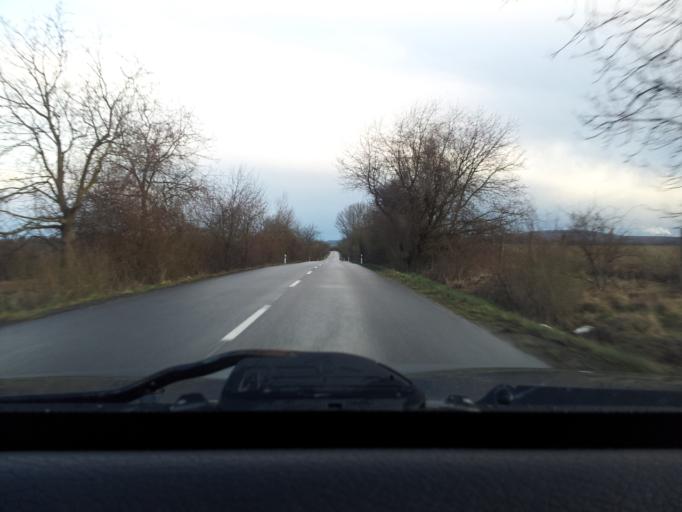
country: SK
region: Nitriansky
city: Tlmace
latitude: 48.3458
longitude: 18.4839
